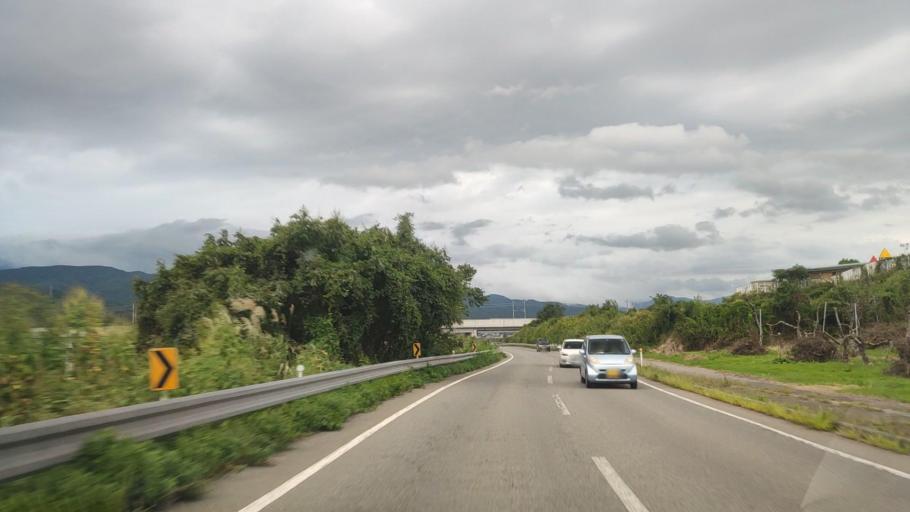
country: JP
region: Nagano
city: Nakano
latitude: 36.7876
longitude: 138.3612
